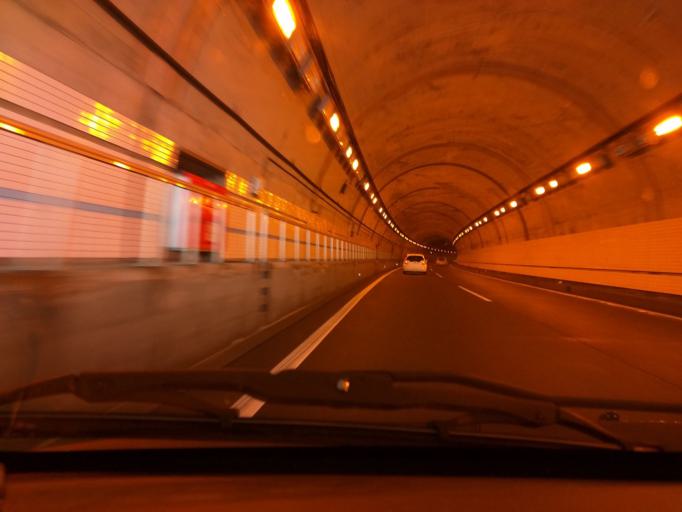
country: JP
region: Niigata
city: Kashiwazaki
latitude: 37.3207
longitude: 138.4565
